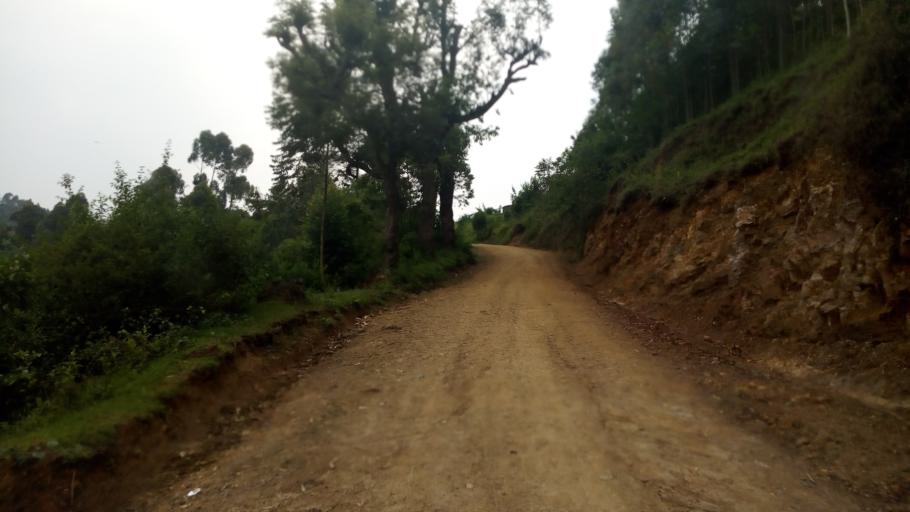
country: UG
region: Western Region
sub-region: Kisoro District
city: Kisoro
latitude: -1.2588
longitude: 29.6305
